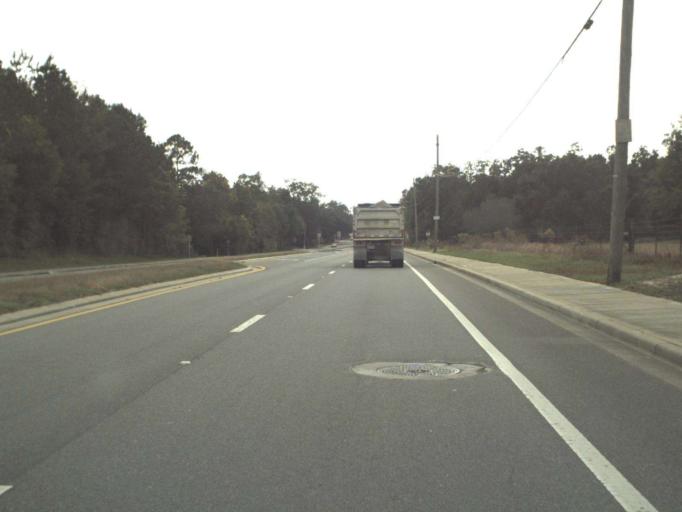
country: US
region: Florida
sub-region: Santa Rosa County
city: Point Baker
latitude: 30.6766
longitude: -87.0542
